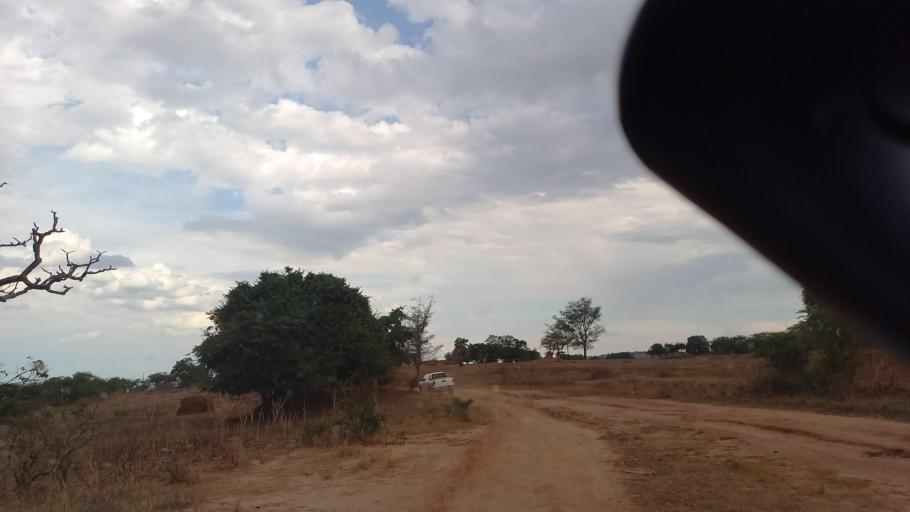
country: ZM
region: Lusaka
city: Kafue
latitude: -16.1353
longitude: 28.0516
